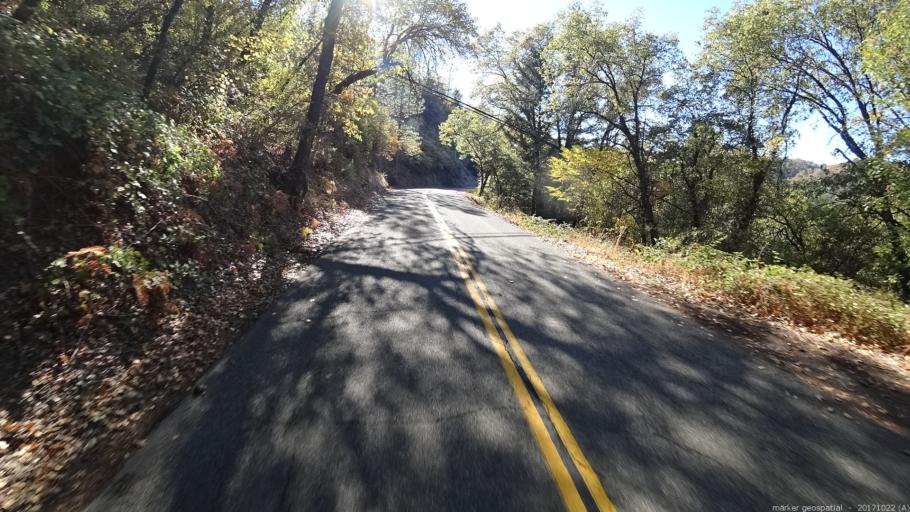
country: US
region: California
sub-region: Shasta County
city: Shasta Lake
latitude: 40.8470
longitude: -122.3433
